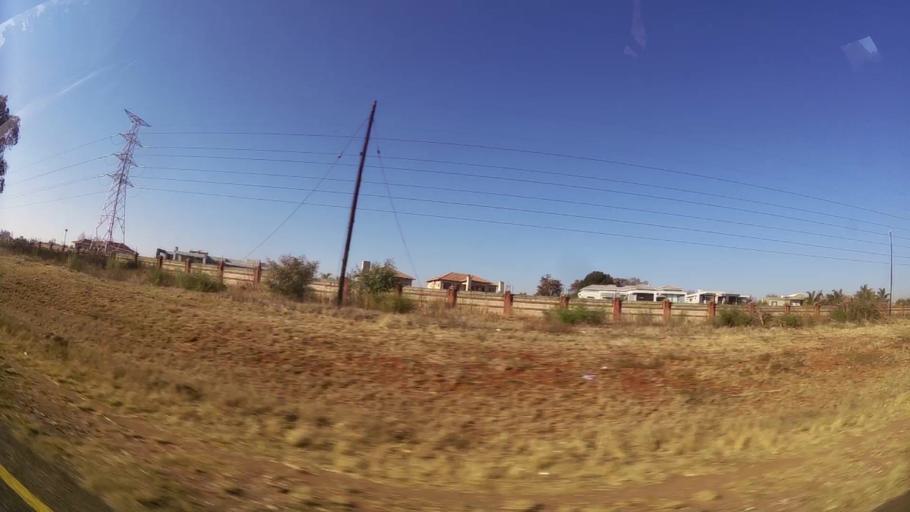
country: ZA
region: Gauteng
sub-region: City of Tshwane Metropolitan Municipality
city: Centurion
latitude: -25.8320
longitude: 28.1412
